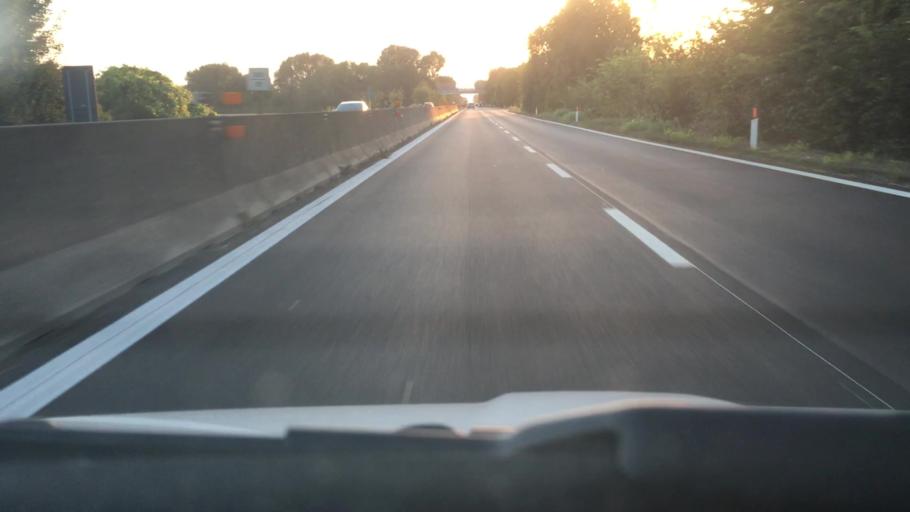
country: IT
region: Emilia-Romagna
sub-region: Provincia di Ferrara
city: Masi-Torello
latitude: 44.7805
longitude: 11.7731
